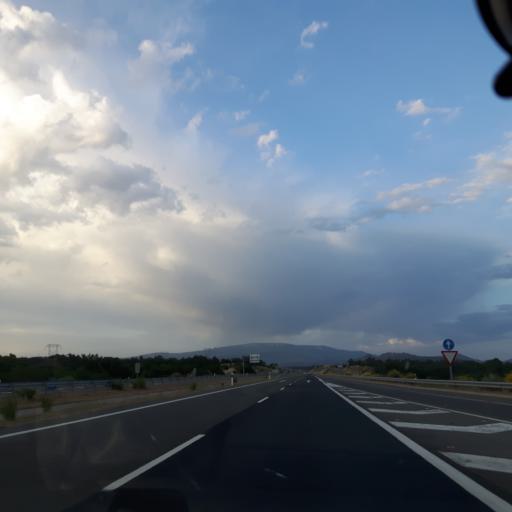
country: ES
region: Castille and Leon
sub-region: Provincia de Salamanca
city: Fuentes de Bejar
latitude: 40.5217
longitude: -5.6723
